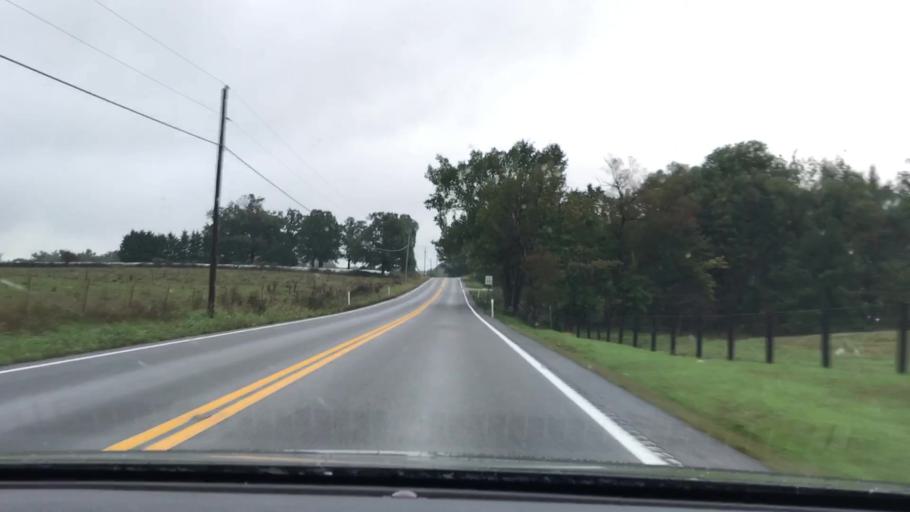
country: US
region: Tennessee
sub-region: Fentress County
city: Grimsley
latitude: 36.1589
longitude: -85.0712
